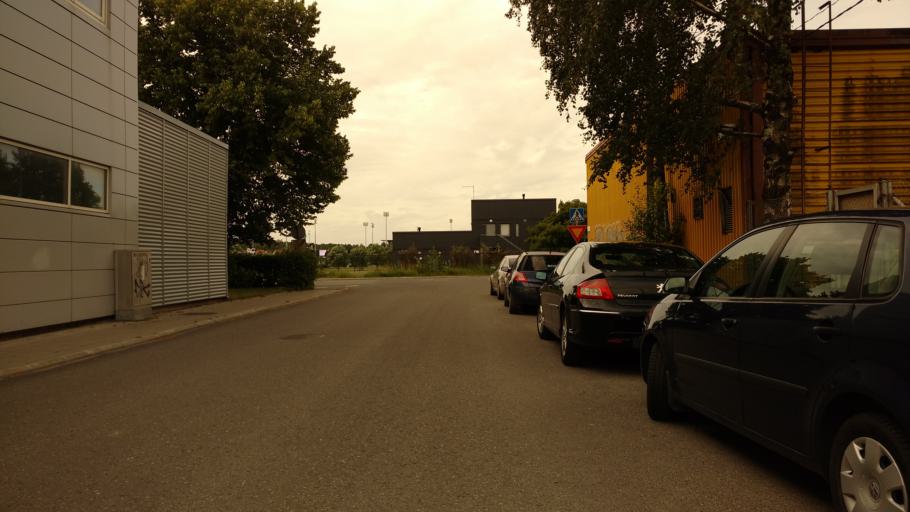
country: FI
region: Varsinais-Suomi
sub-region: Turku
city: Turku
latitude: 60.4474
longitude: 22.2978
